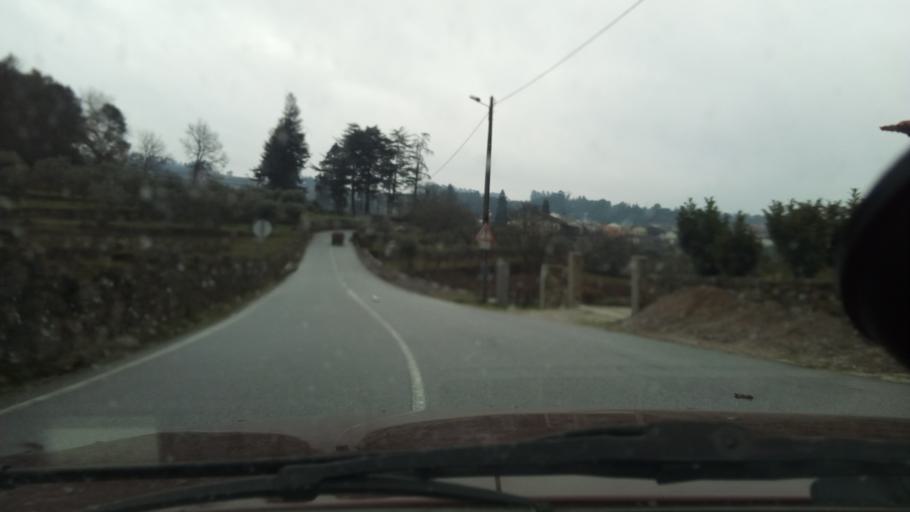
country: PT
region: Viseu
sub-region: Mangualde
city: Mangualde
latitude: 40.6114
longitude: -7.8149
